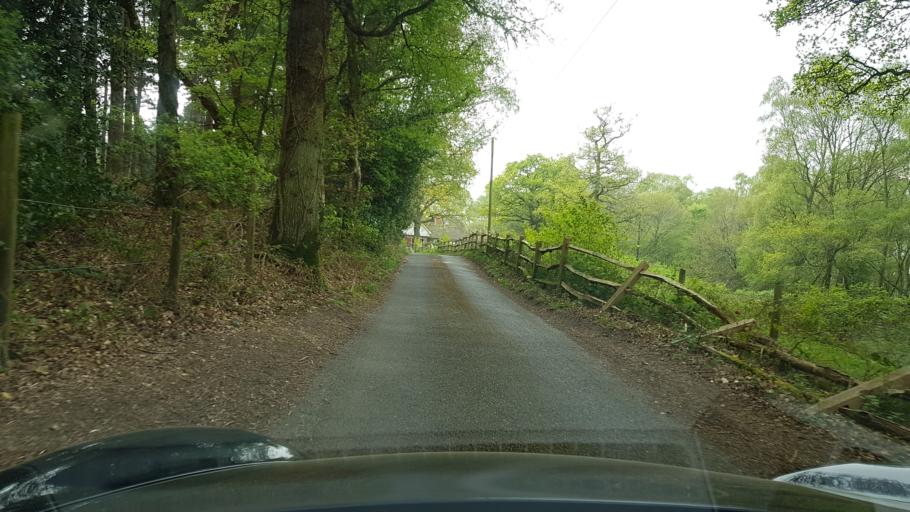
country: GB
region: England
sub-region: Surrey
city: East Horsley
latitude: 51.2422
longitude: -0.4497
